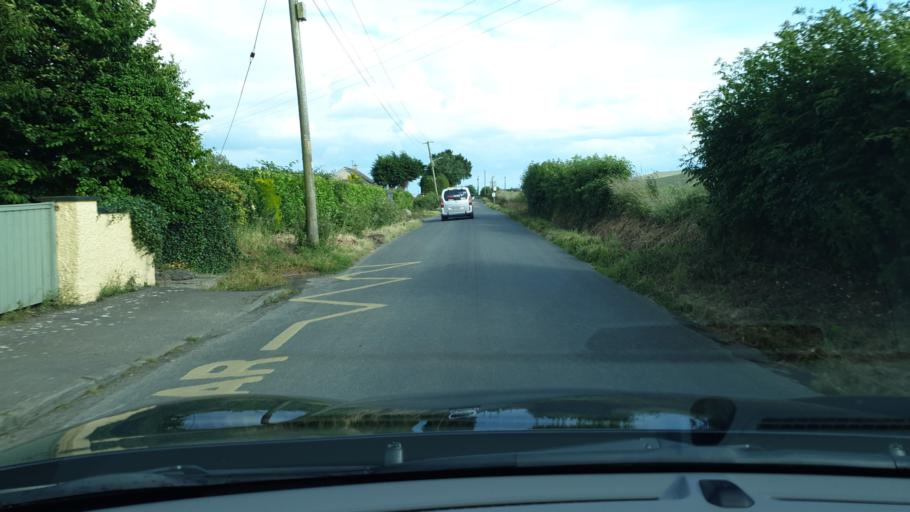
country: IE
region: Leinster
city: Lusk
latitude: 53.5646
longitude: -6.1477
